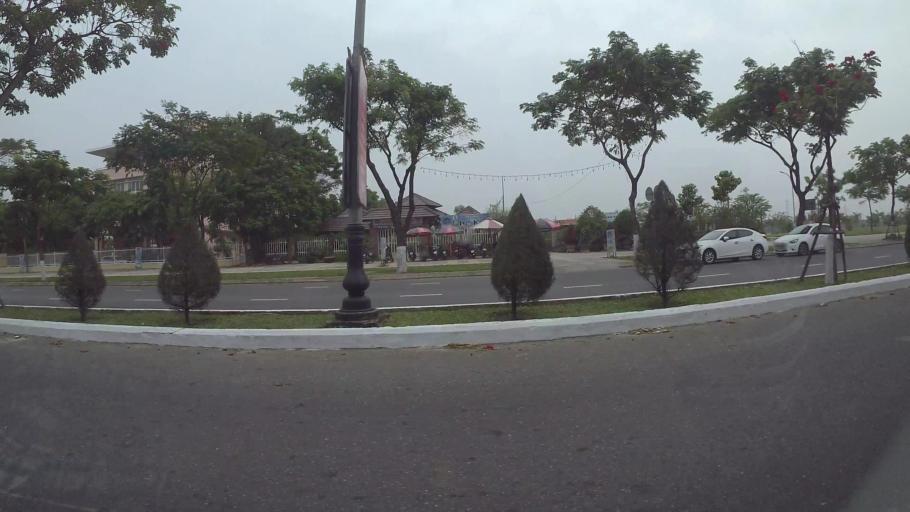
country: VN
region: Da Nang
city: Cam Le
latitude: 16.0279
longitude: 108.2136
